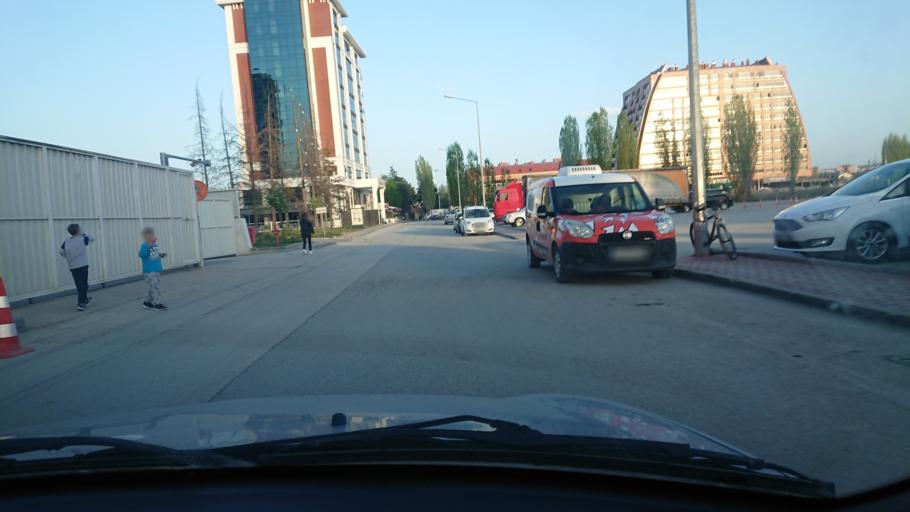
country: TR
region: Eskisehir
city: Eskisehir
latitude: 39.7834
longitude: 30.4978
